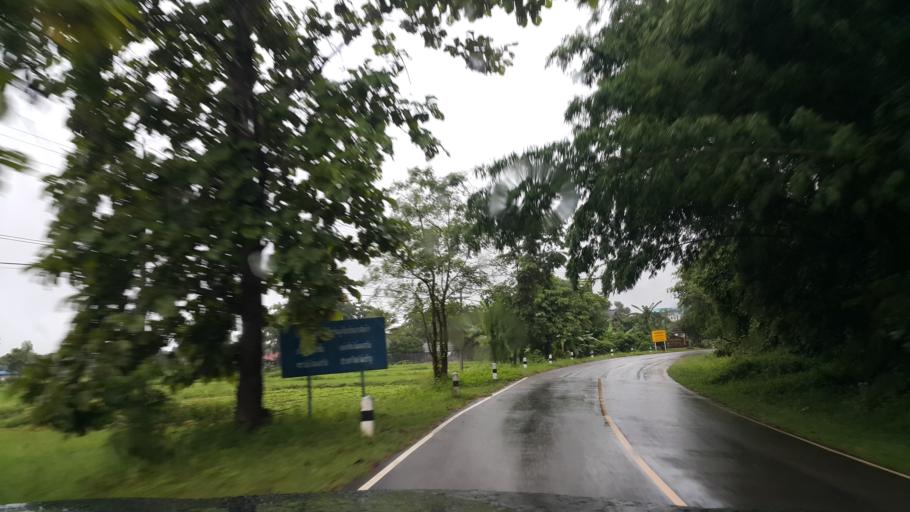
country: TH
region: Phayao
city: Phu Sang
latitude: 19.5885
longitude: 100.3674
